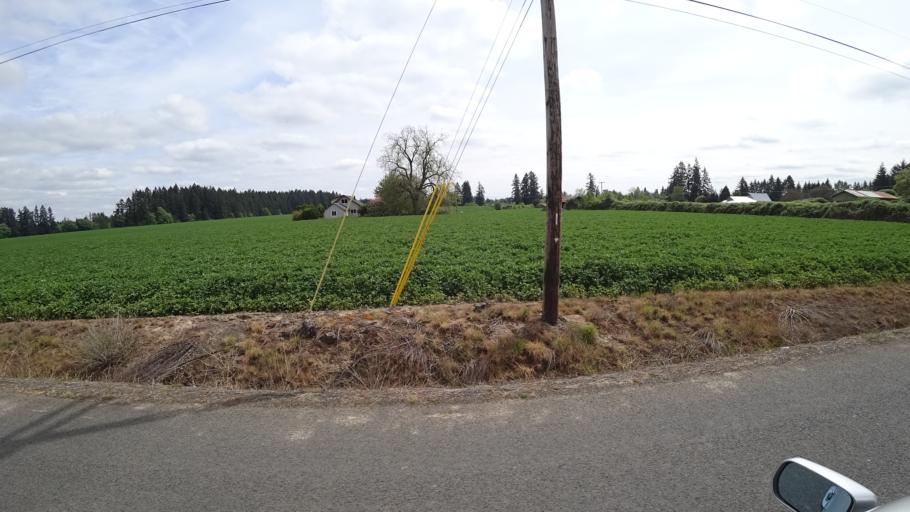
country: US
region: Oregon
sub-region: Washington County
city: Hillsboro
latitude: 45.5352
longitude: -123.0108
